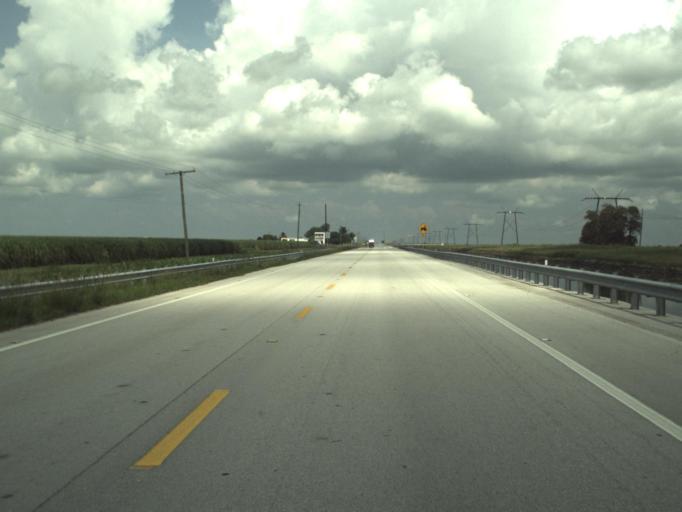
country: US
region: Florida
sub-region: Palm Beach County
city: Pahokee
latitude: 26.7585
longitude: -80.4916
